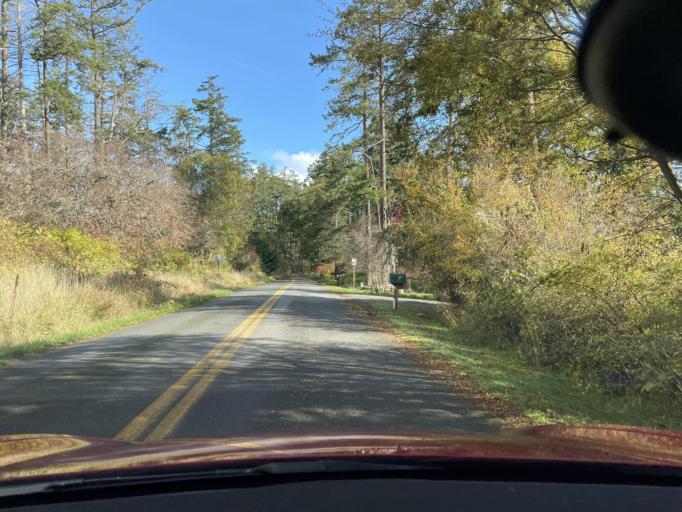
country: US
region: Washington
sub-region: San Juan County
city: Friday Harbor
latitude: 48.5040
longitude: -123.0221
